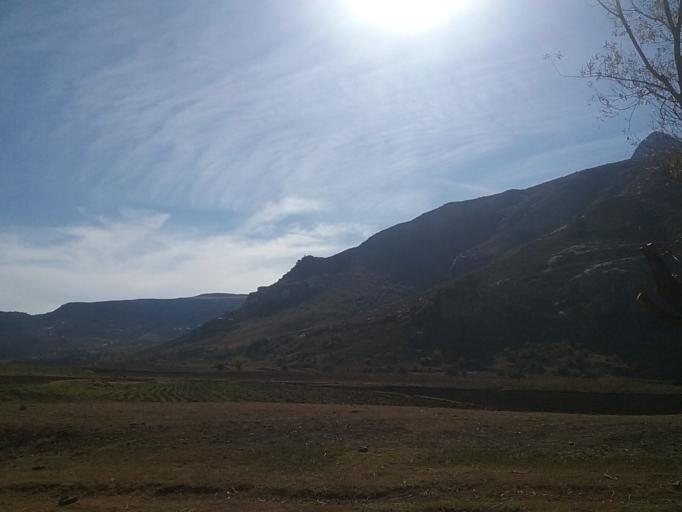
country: LS
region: Berea
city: Teyateyaneng
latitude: -29.2507
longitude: 27.9151
